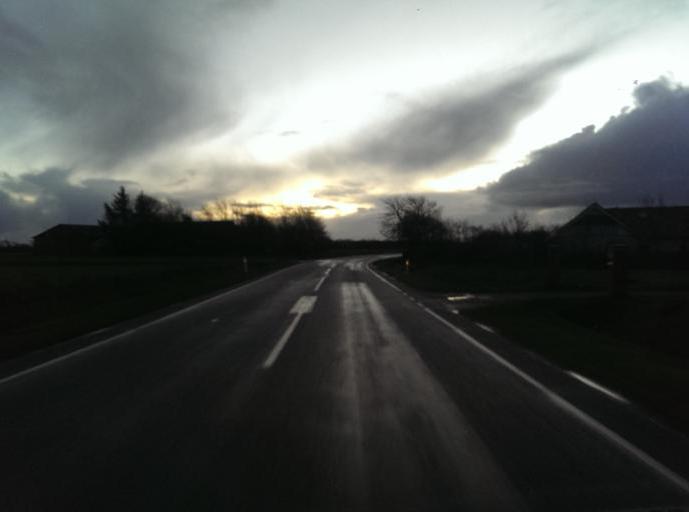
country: DK
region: South Denmark
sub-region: Esbjerg Kommune
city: Bramming
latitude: 55.4317
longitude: 8.6751
